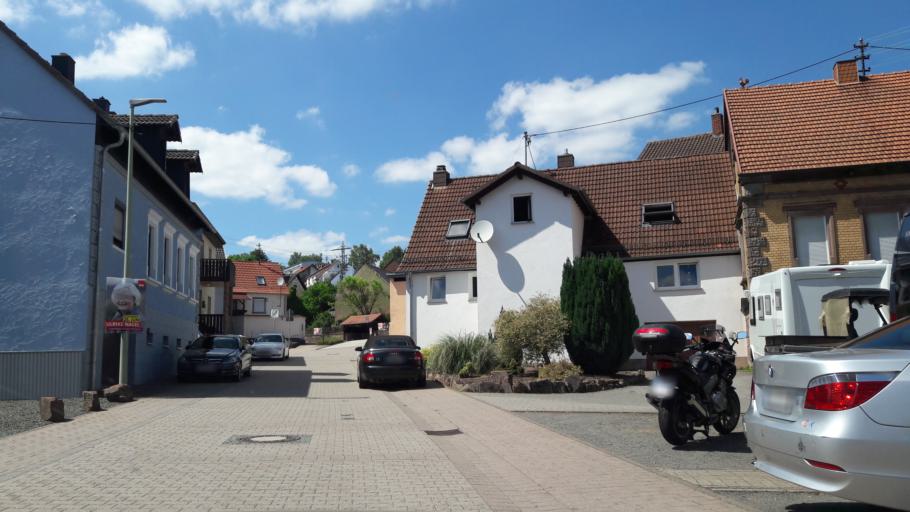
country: DE
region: Rheinland-Pfalz
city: Dunzweiler
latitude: 49.4153
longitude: 7.3061
